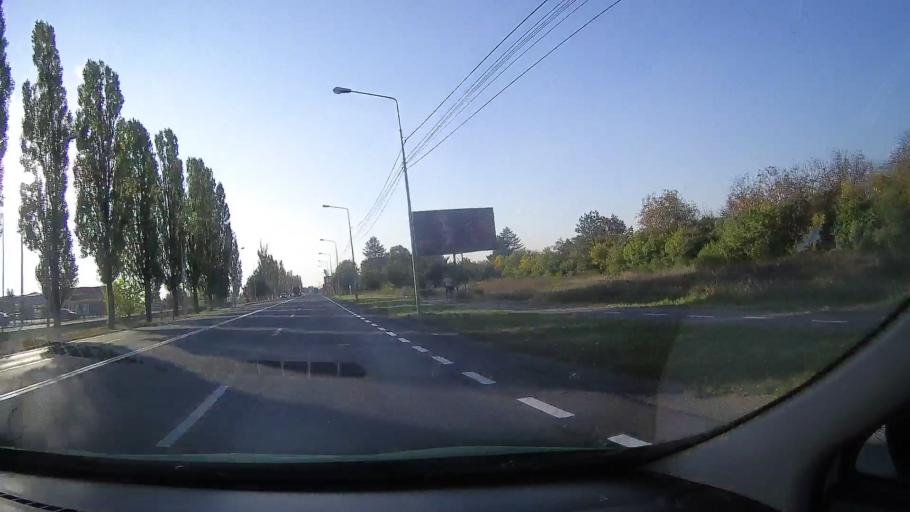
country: RO
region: Bihor
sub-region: Comuna Bors
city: Santion
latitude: 47.1000
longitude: 21.8520
